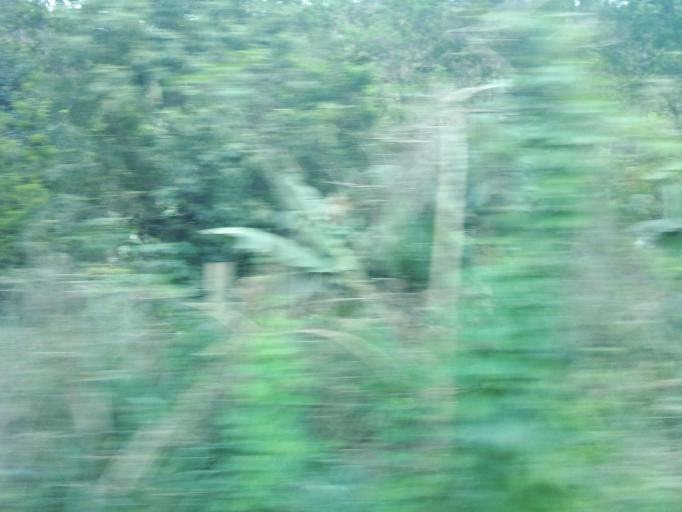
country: BR
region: Minas Gerais
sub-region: Coronel Fabriciano
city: Coronel Fabriciano
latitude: -19.5372
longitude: -42.6742
